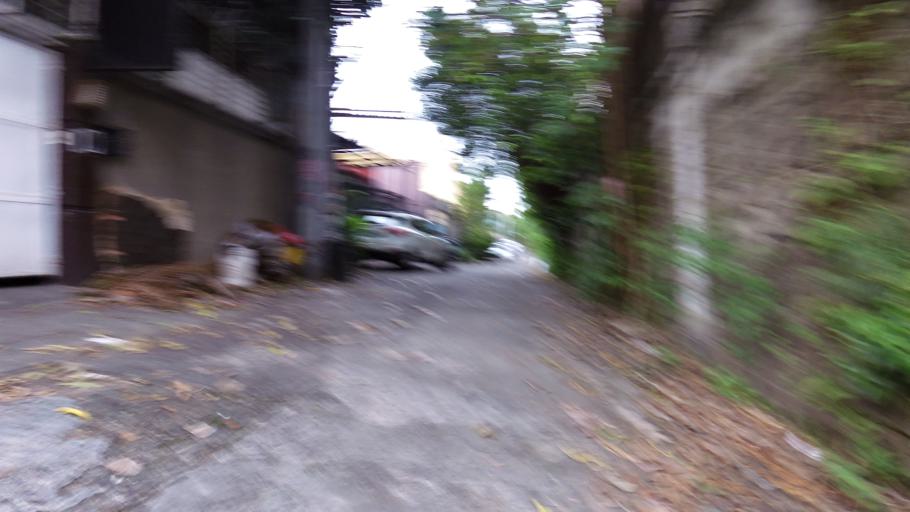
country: PH
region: Metro Manila
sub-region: San Juan
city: San Juan
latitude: 14.6112
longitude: 121.0468
